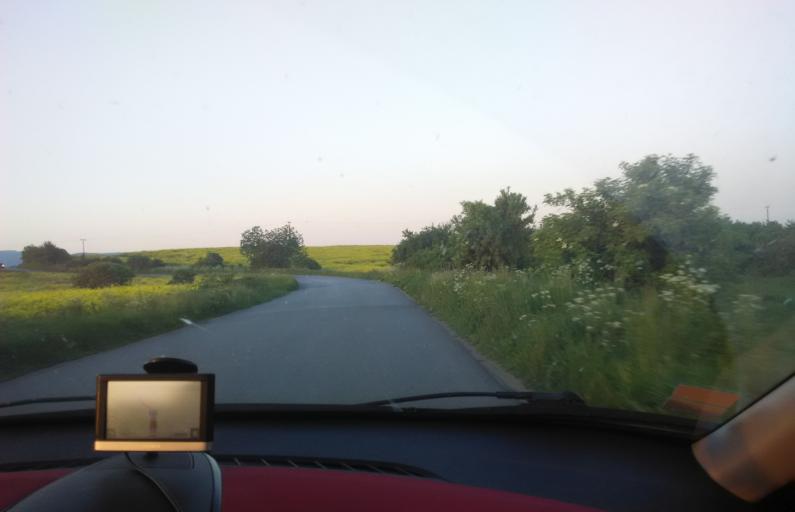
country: SK
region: Presovsky
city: Sabinov
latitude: 49.0679
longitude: 21.0726
